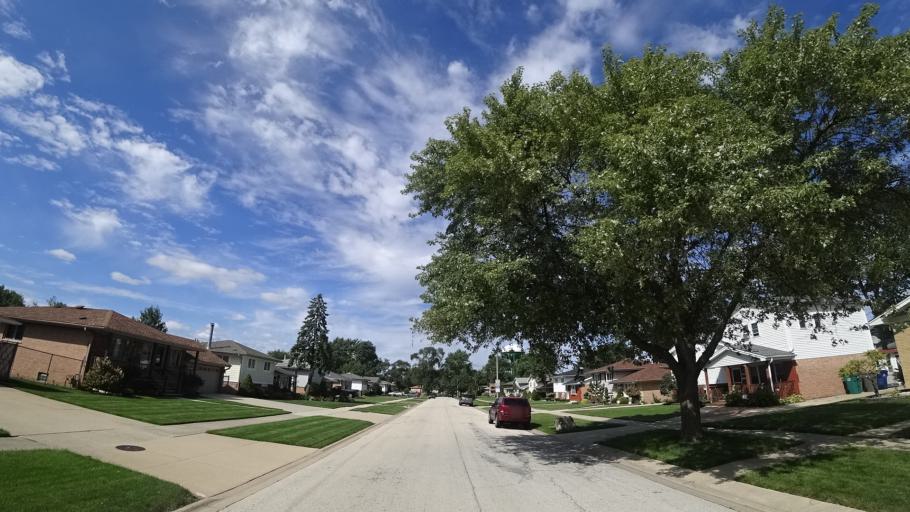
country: US
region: Illinois
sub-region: Cook County
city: Chicago Ridge
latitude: 41.6990
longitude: -87.7821
